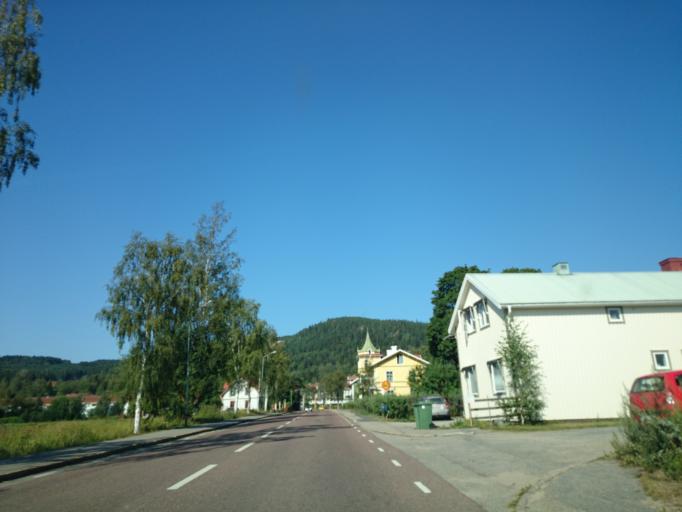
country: SE
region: Gaevleborg
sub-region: Ljusdals Kommun
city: Jaervsoe
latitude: 61.7130
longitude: 16.1759
